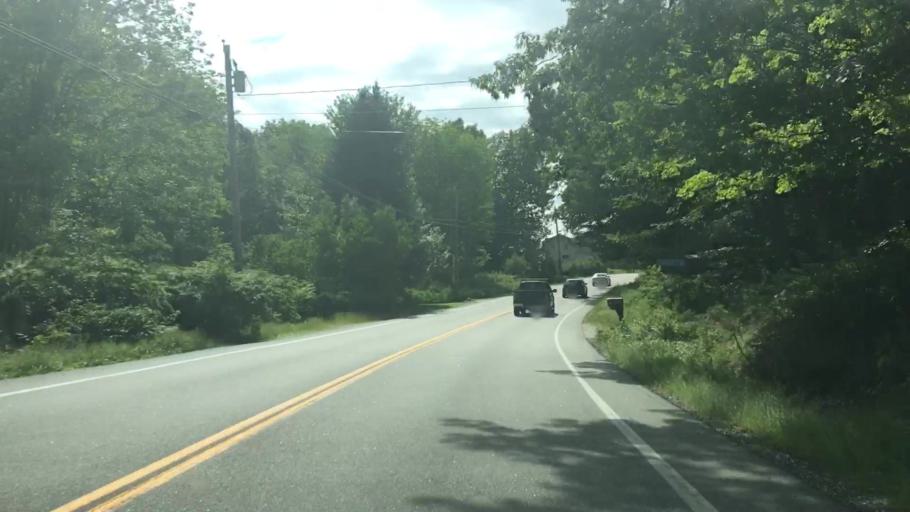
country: US
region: Maine
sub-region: Cumberland County
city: Raymond
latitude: 43.9869
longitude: -70.4737
